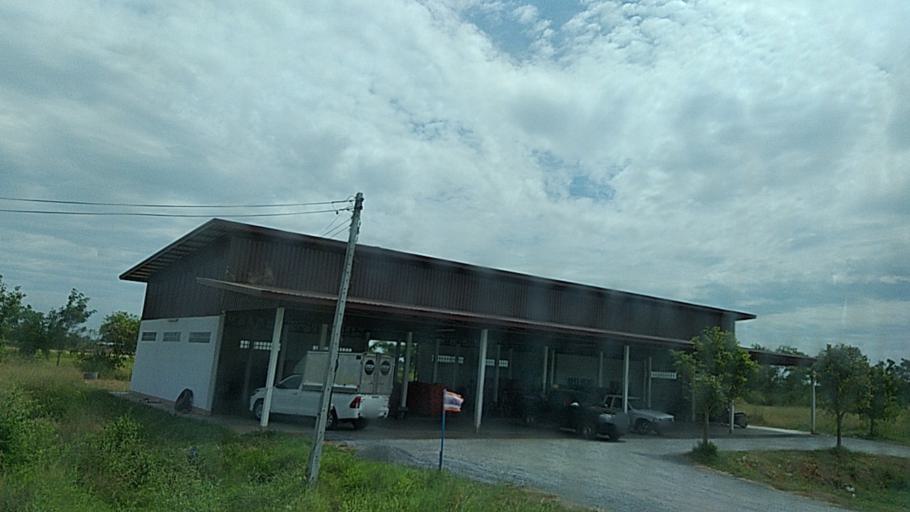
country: TH
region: Maha Sarakham
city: Chiang Yuen
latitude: 16.3836
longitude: 103.1030
